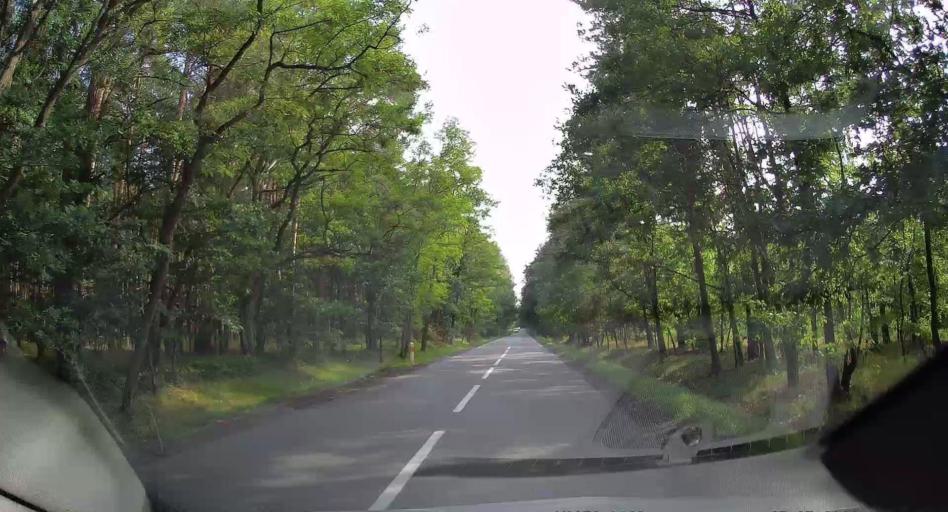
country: PL
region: Lodz Voivodeship
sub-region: Powiat tomaszowski
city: Rzeczyca
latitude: 51.5720
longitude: 20.2770
